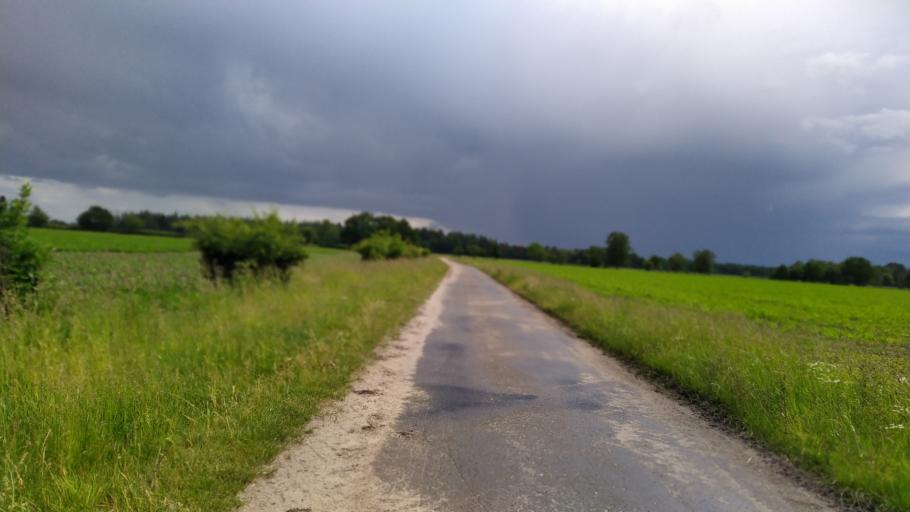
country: DE
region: Lower Saxony
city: Kutenholz
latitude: 53.4636
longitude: 9.3453
